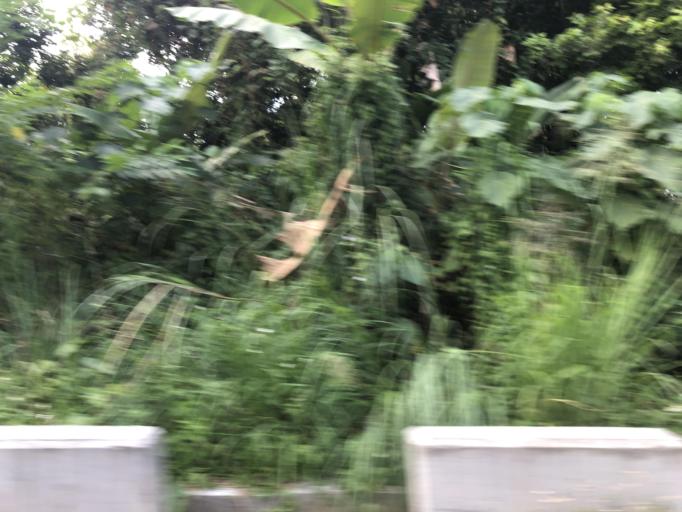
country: TW
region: Taiwan
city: Yujing
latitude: 23.0150
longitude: 120.4169
